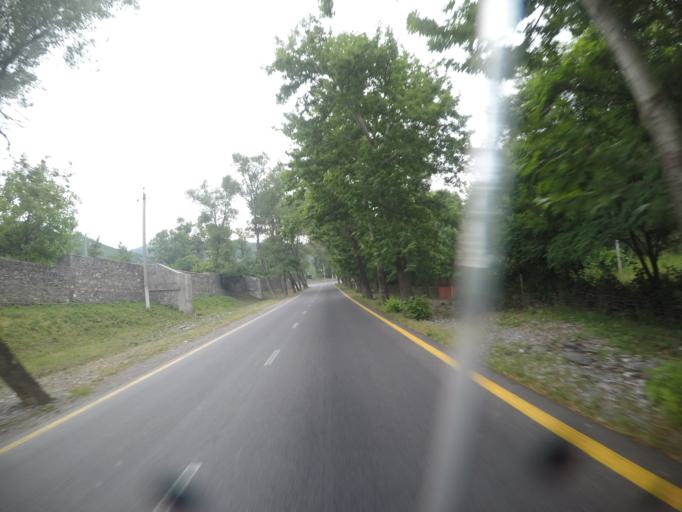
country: AZ
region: Shaki City
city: Sheki
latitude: 41.2403
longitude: 47.1853
